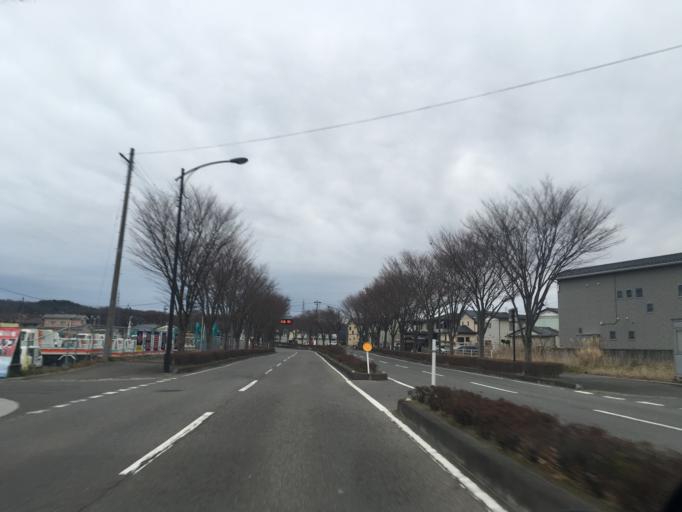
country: JP
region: Fukushima
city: Koriyama
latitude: 37.3959
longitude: 140.4063
